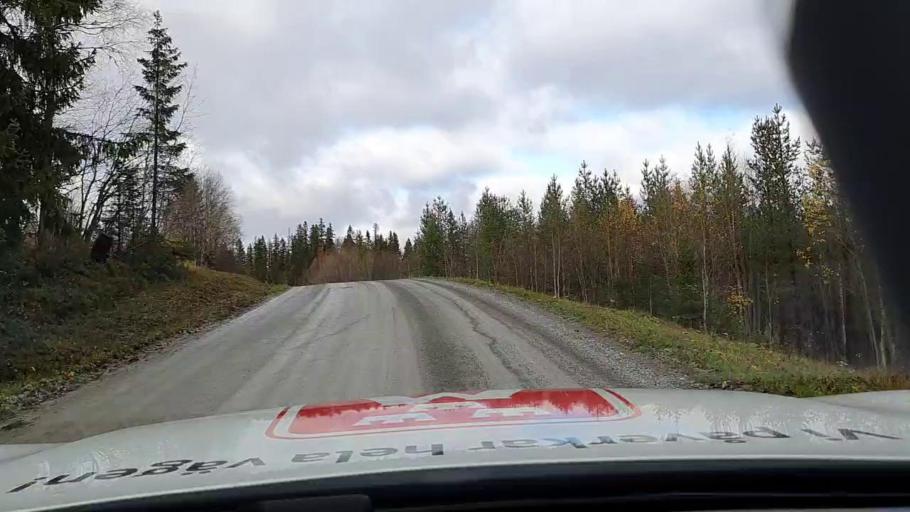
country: SE
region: Jaemtland
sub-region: Bergs Kommun
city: Hoverberg
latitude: 63.0029
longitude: 14.1347
